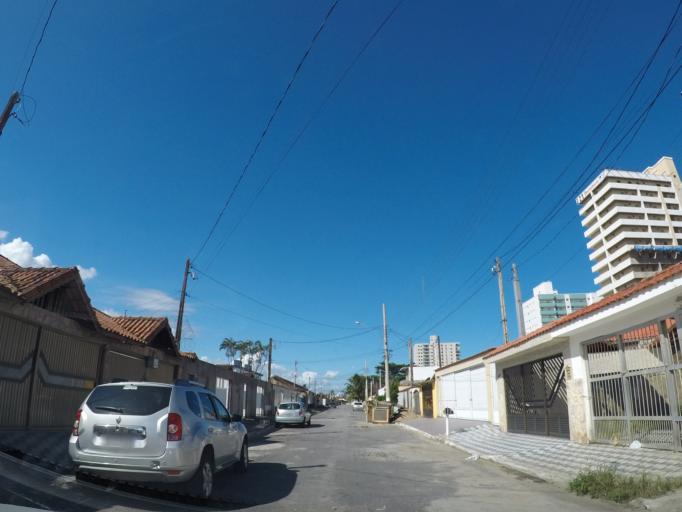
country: BR
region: Sao Paulo
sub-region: Mongagua
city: Mongagua
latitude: -24.0620
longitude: -46.5520
